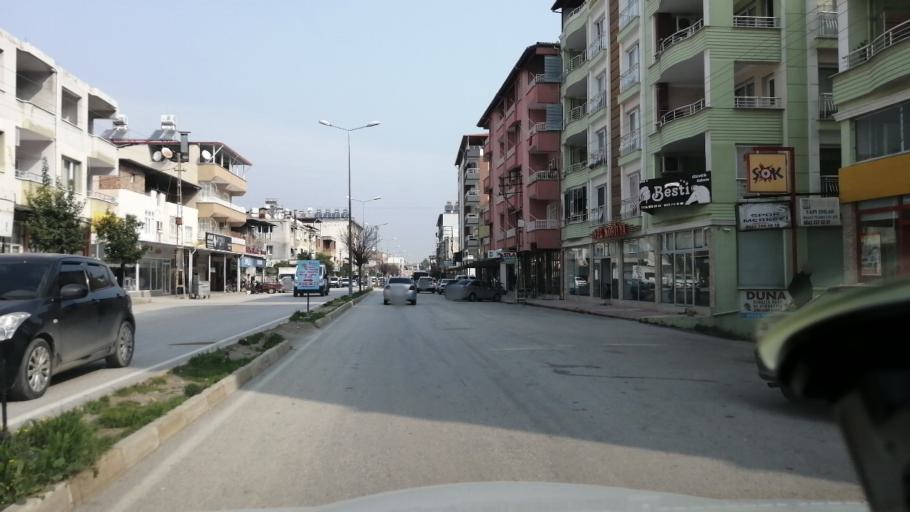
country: TR
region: Hatay
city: Serinyol
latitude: 36.3598
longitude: 36.2106
